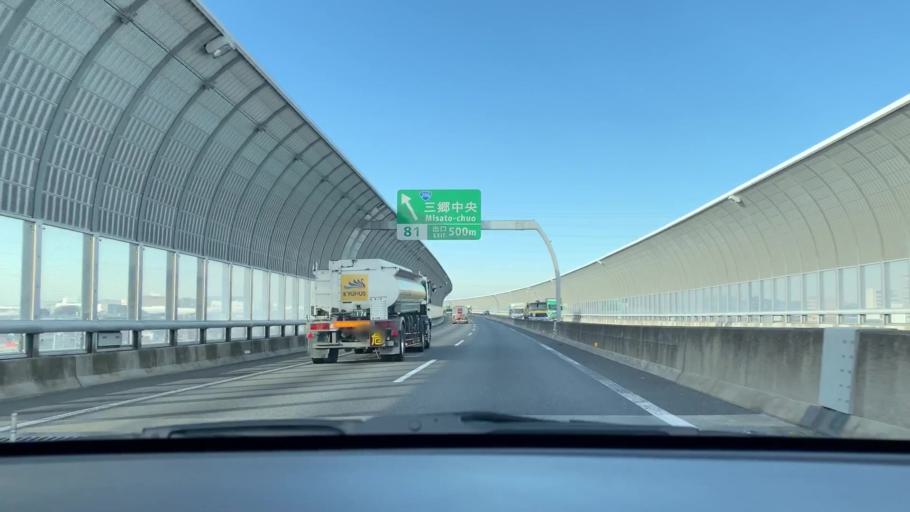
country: JP
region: Saitama
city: Yashio-shi
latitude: 35.8193
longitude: 139.8739
